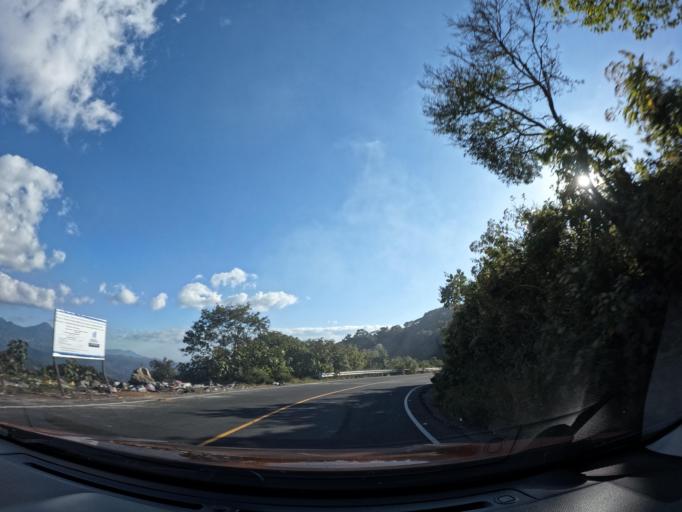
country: GT
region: Sacatepequez
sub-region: Municipio de Santa Maria de Jesus
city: Santa Maria de Jesus
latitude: 14.4671
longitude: -90.6937
